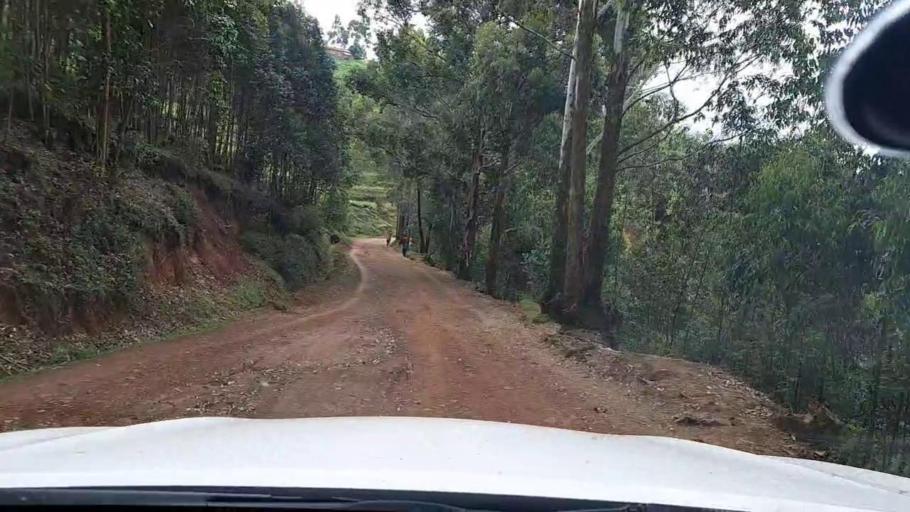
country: RW
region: Western Province
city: Kibuye
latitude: -2.1697
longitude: 29.4252
